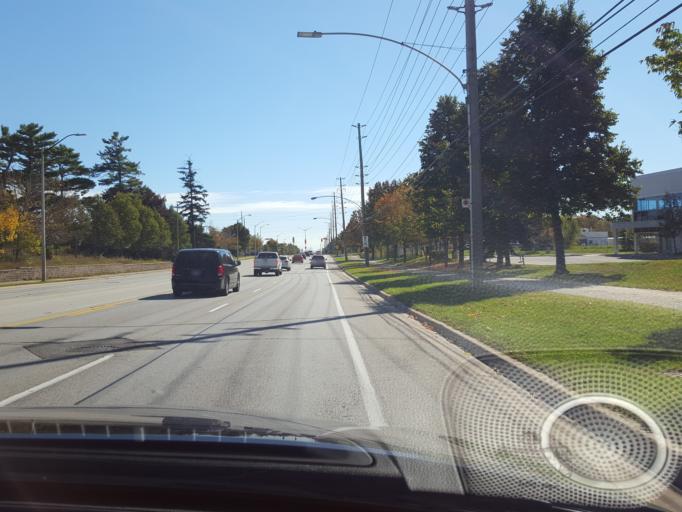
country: CA
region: Ontario
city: Burlington
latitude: 43.3887
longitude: -79.7832
